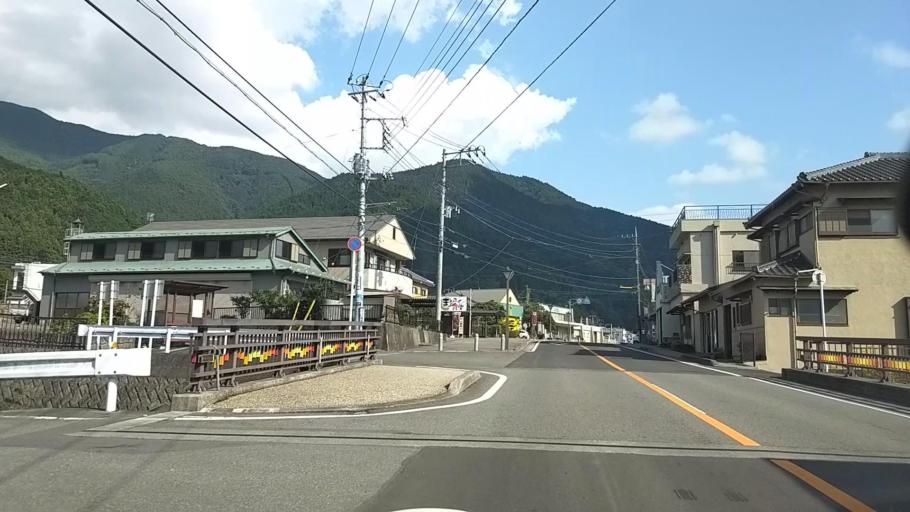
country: JP
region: Shizuoka
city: Fujinomiya
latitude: 35.2825
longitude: 138.4637
